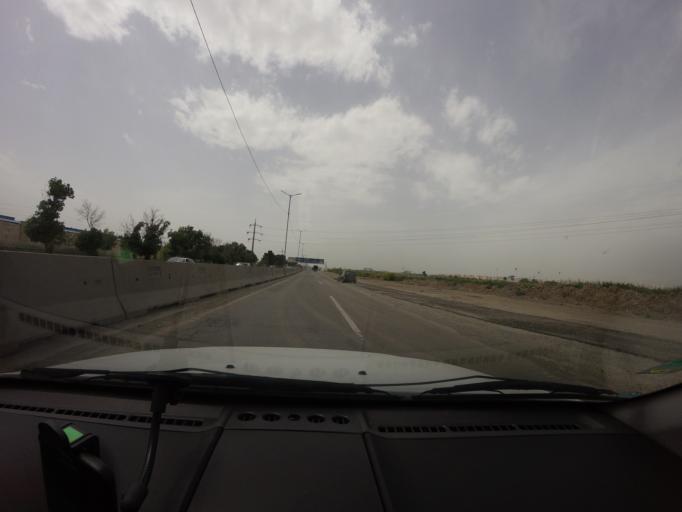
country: IR
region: Tehran
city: Eslamshahr
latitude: 35.5117
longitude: 51.2552
